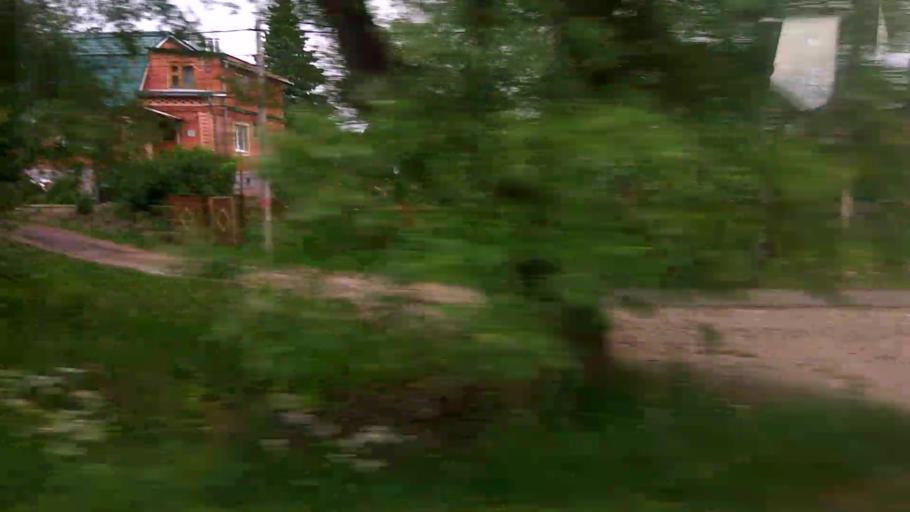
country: RU
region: Moskovskaya
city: Lukhovitsy
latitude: 54.9286
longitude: 39.0025
